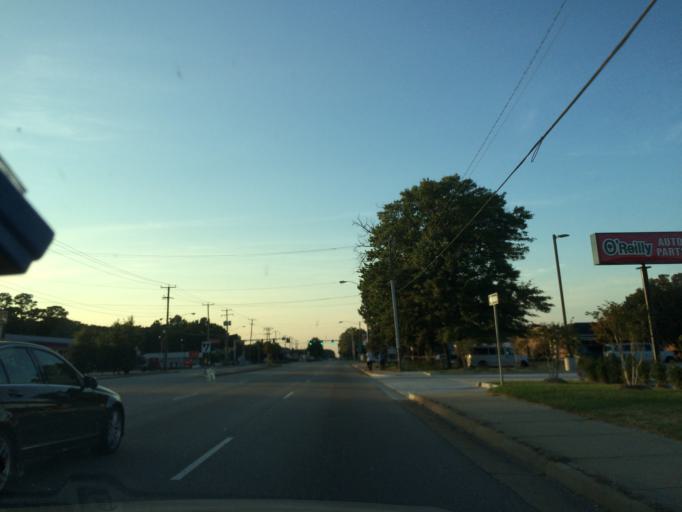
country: US
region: Virginia
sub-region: City of Newport News
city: Newport News
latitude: 37.0539
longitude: -76.4624
